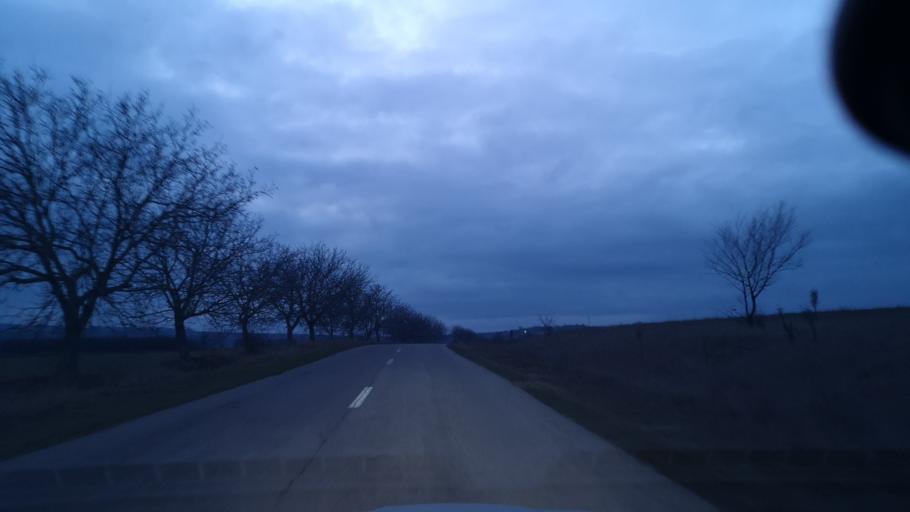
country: MD
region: Telenesti
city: Cocieri
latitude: 47.3076
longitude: 28.9821
